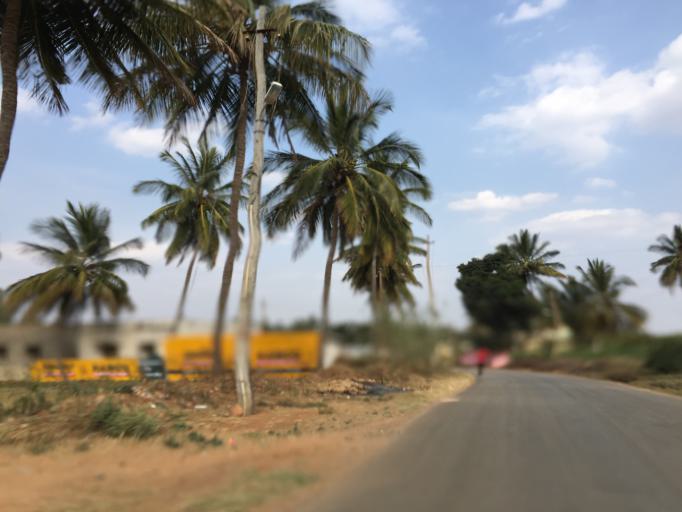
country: IN
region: Karnataka
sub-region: Chikkaballapur
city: Chik Ballapur
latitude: 13.3843
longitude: 77.6929
